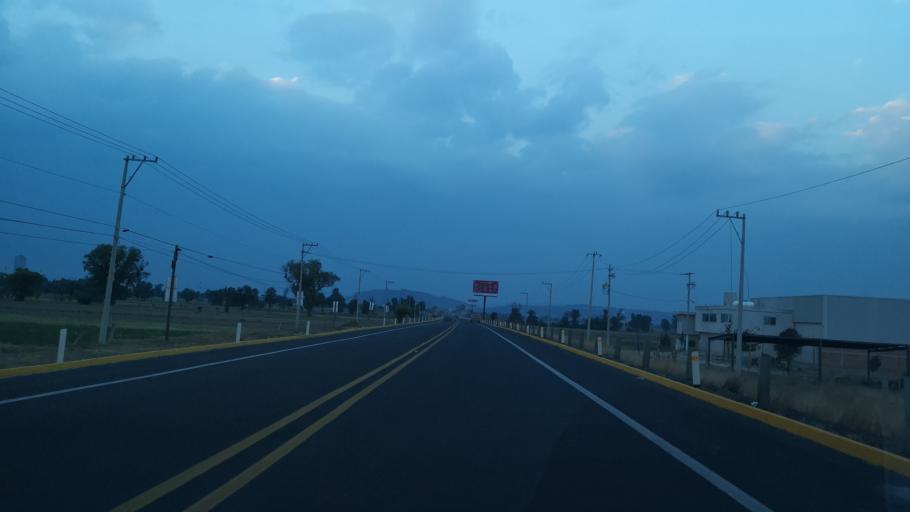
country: MX
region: Puebla
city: Santa Ana Xalmimilulco
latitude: 19.1945
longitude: -98.3660
